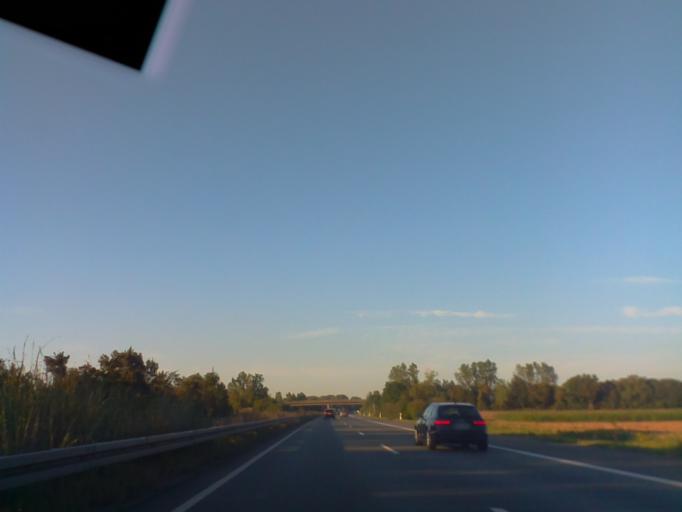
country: DE
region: Hesse
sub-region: Regierungsbezirk Darmstadt
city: Alsbach-Hahnlein
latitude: 49.7458
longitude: 8.5923
